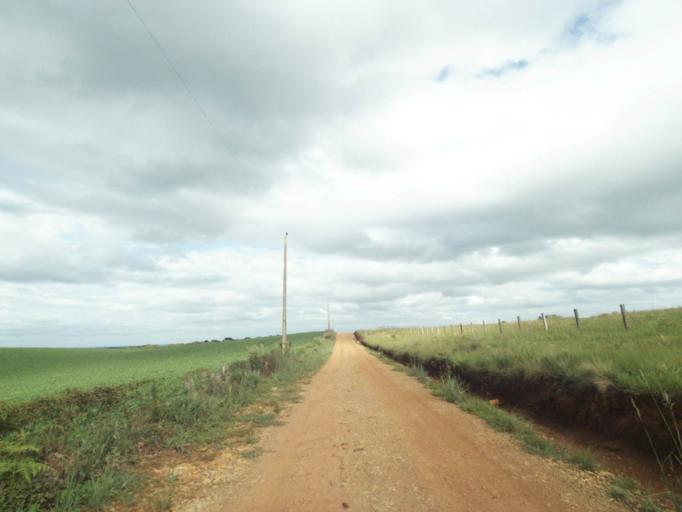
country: BR
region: Rio Grande do Sul
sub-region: Lagoa Vermelha
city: Lagoa Vermelha
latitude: -28.2024
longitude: -51.5145
